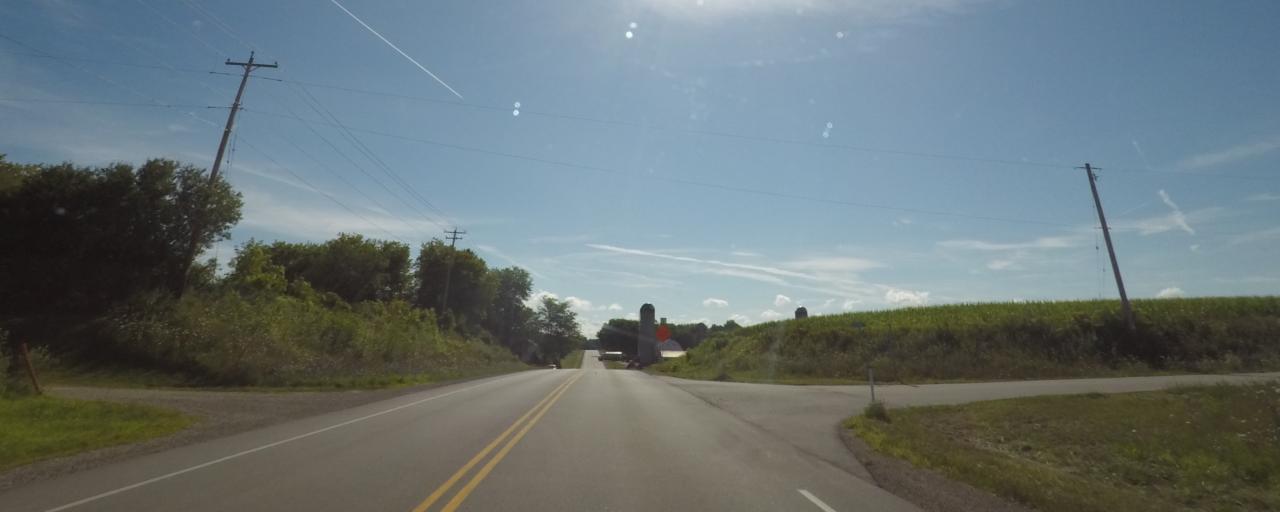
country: US
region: Wisconsin
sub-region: Jefferson County
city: Johnson Creek
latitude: 43.0756
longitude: -88.7276
